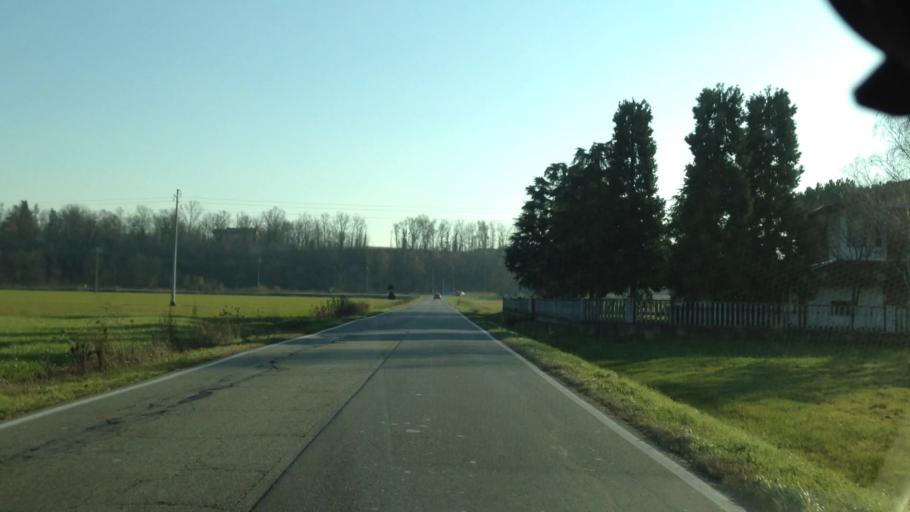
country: IT
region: Piedmont
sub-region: Provincia di Alessandria
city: Felizzano
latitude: 44.8758
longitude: 8.4451
